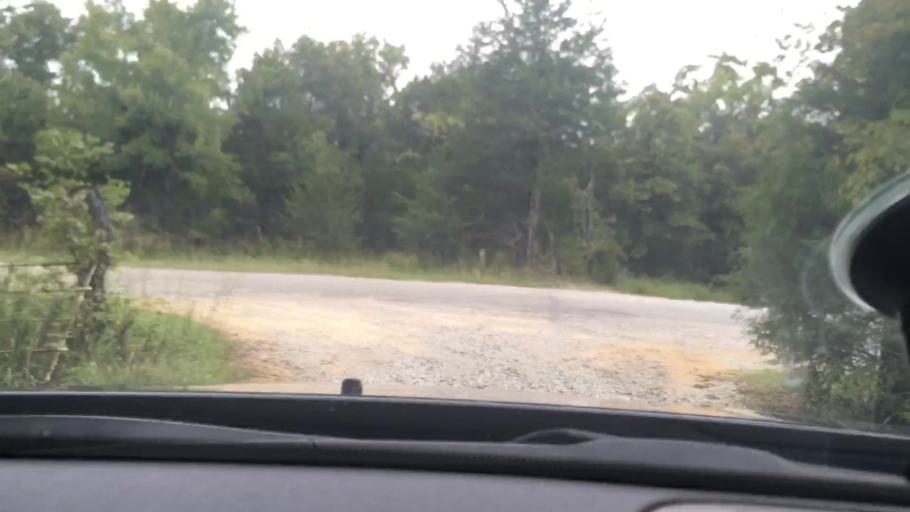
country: US
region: Oklahoma
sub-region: Pontotoc County
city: Byng
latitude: 34.8180
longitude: -96.5340
